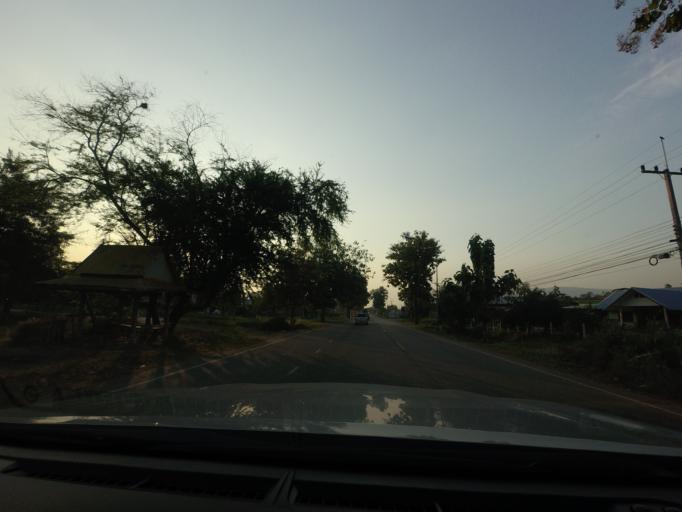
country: TH
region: Phitsanulok
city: Wang Thong
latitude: 16.7054
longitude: 100.5064
